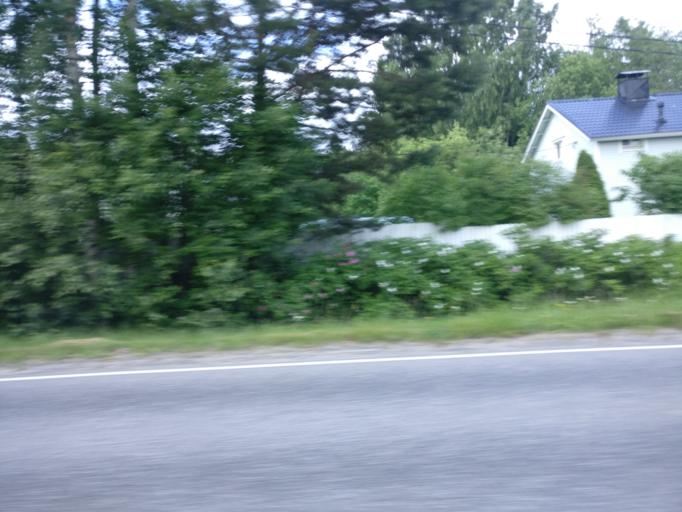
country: FI
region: Southern Savonia
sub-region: Savonlinna
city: Savonlinna
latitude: 61.8773
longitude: 28.9491
